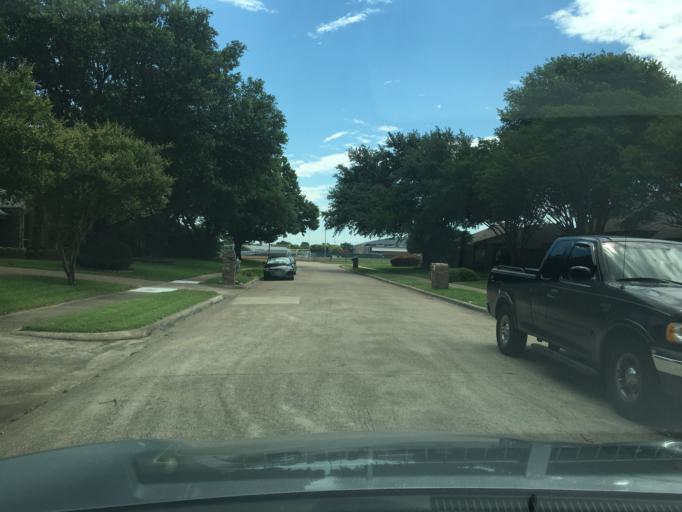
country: US
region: Texas
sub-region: Dallas County
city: Richardson
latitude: 32.9354
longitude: -96.6964
